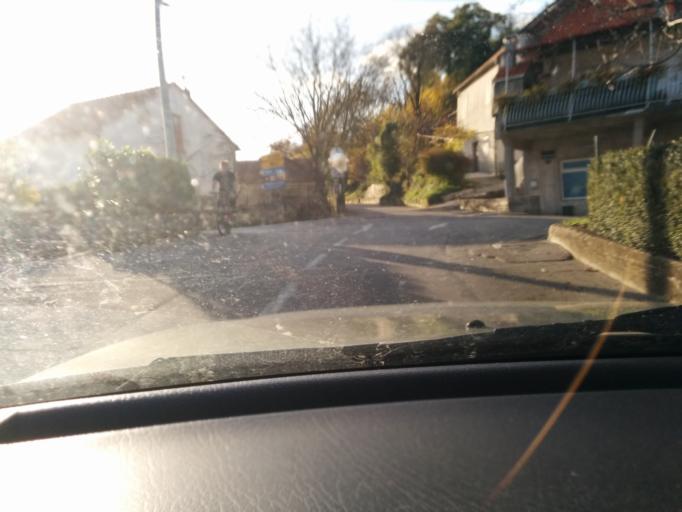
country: HR
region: Splitsko-Dalmatinska
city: Sinj
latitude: 43.7072
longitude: 16.6376
